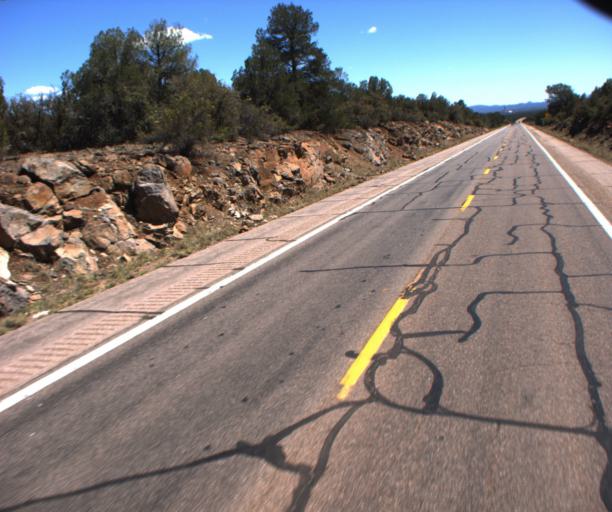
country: US
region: Arizona
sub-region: Yavapai County
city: Paulden
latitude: 35.0657
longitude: -112.4002
